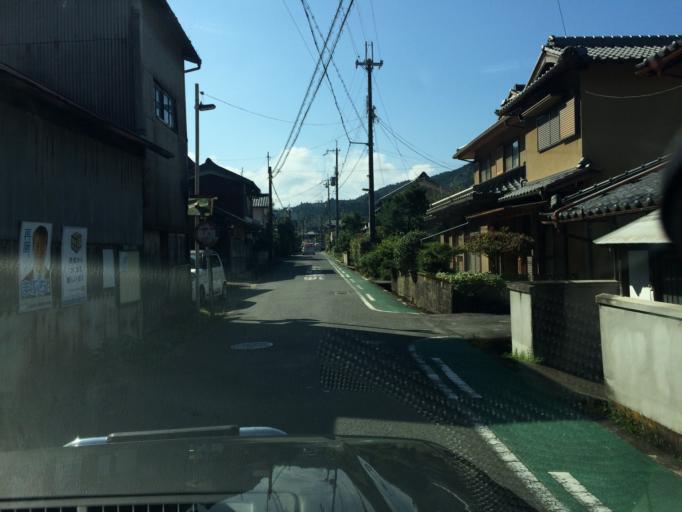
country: JP
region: Nara
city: Nara-shi
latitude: 34.7362
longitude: 135.9522
